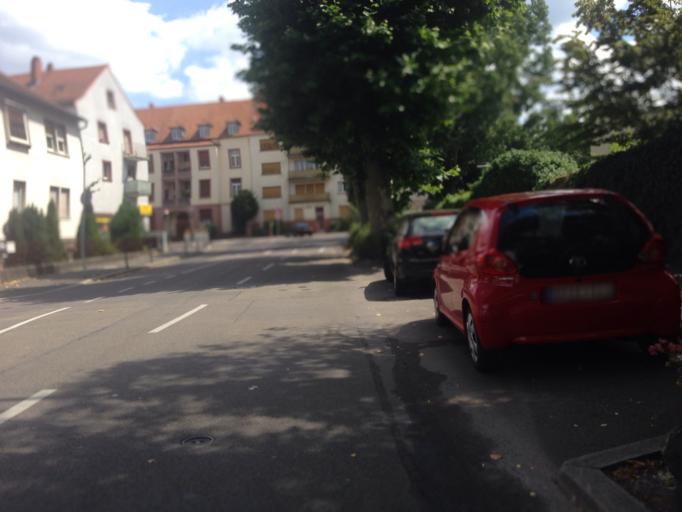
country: DE
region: Hesse
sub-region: Regierungsbezirk Darmstadt
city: Hanau am Main
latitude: 50.1347
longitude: 8.9217
